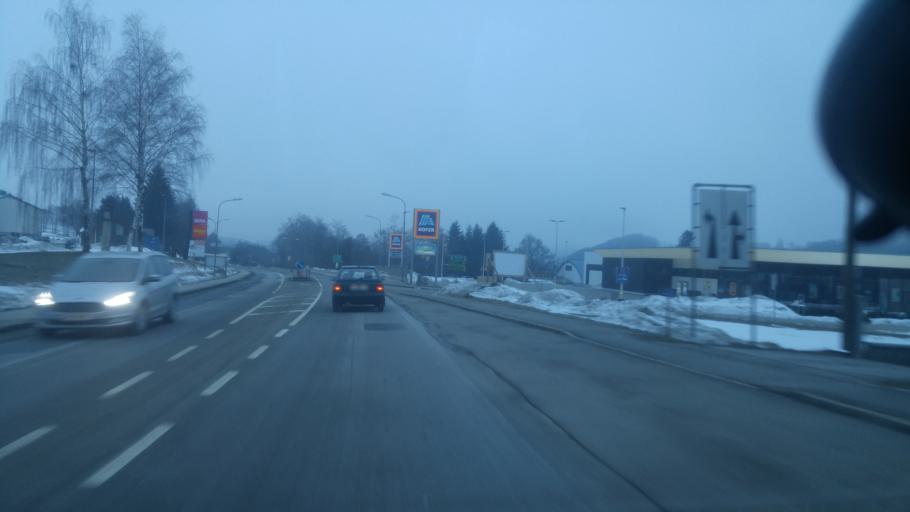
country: AT
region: Lower Austria
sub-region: Politischer Bezirk Lilienfeld
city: Hainfeld
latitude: 48.0392
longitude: 15.7602
